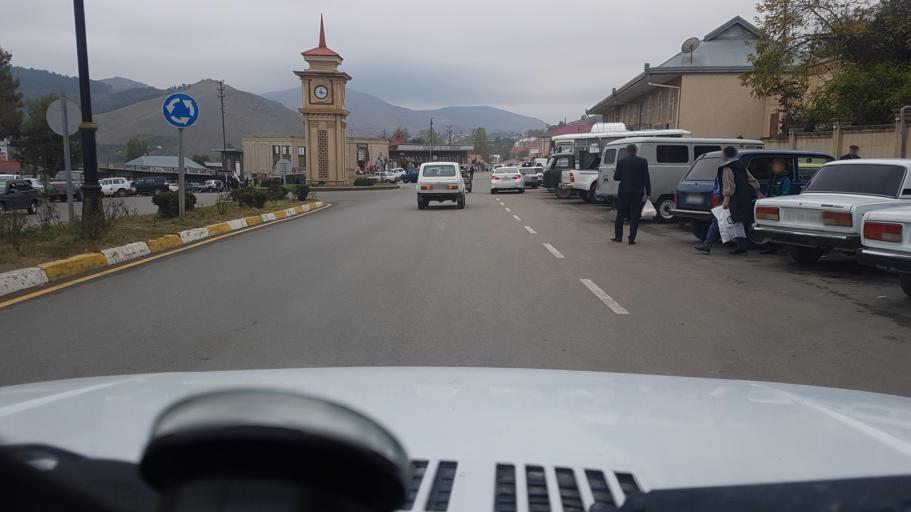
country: AZ
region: Gadabay Rayon
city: Kyadabek
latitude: 40.5752
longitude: 45.8079
